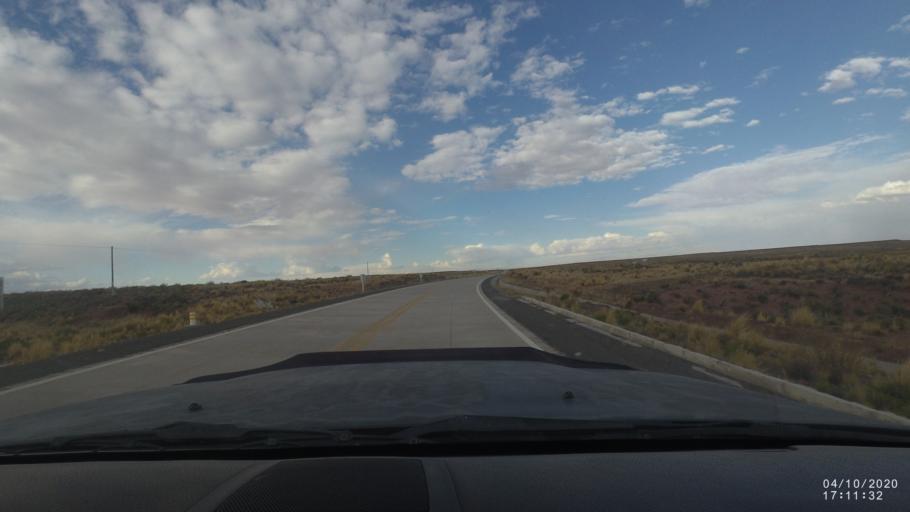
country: BO
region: Oruro
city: Oruro
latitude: -18.3189
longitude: -67.5755
